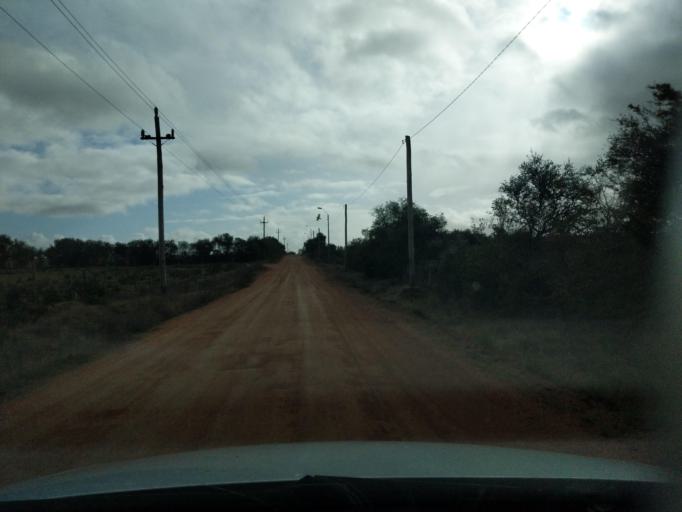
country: UY
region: Florida
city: Florida
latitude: -34.0653
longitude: -56.2184
